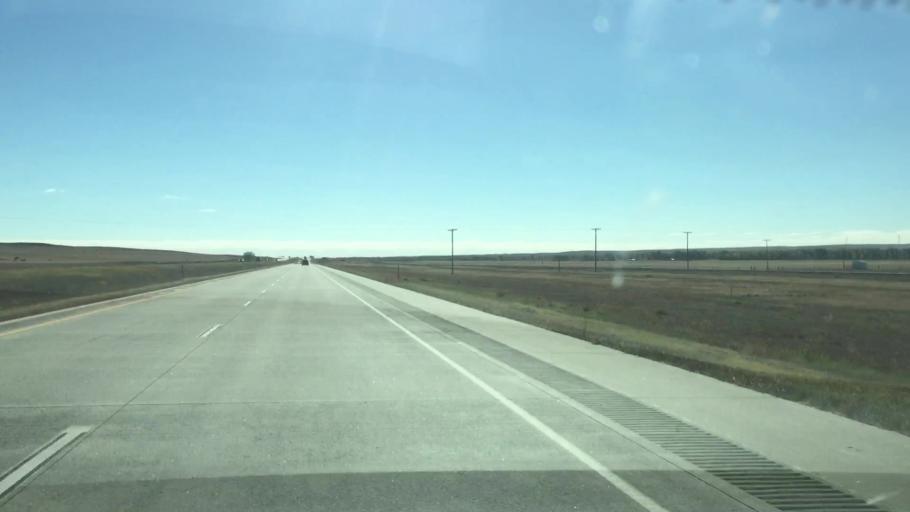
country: US
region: Colorado
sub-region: Lincoln County
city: Limon
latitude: 39.2993
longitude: -103.8096
